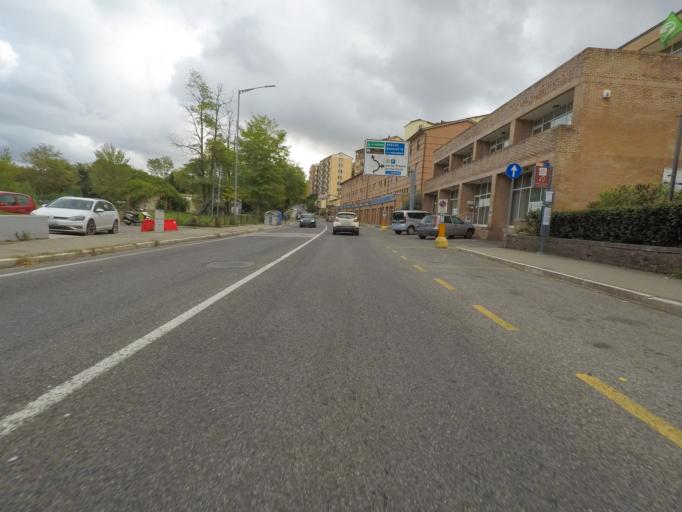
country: IT
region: Tuscany
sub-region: Provincia di Siena
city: Siena
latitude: 43.3279
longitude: 11.3302
